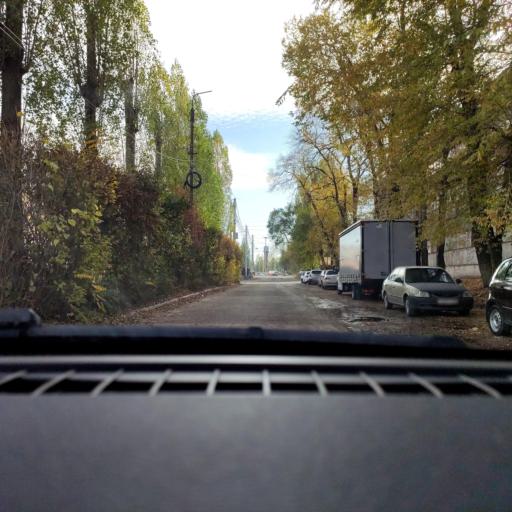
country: RU
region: Voronezj
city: Maslovka
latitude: 51.6470
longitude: 39.2941
